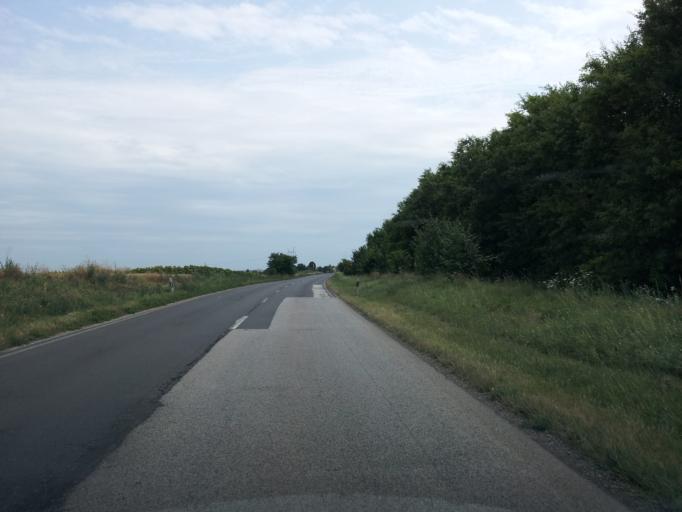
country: HU
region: Fejer
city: Lepseny
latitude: 46.9648
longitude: 18.2107
